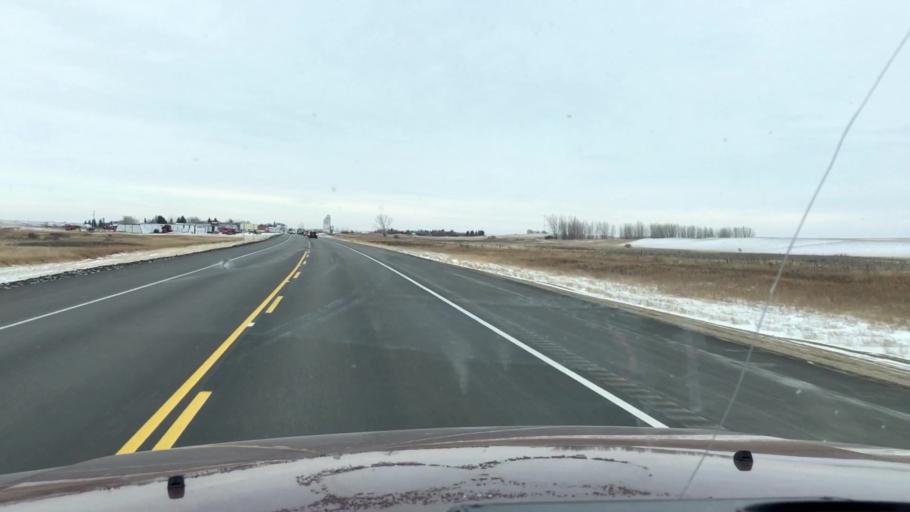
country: CA
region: Saskatchewan
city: Moose Jaw
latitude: 50.8581
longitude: -105.5821
